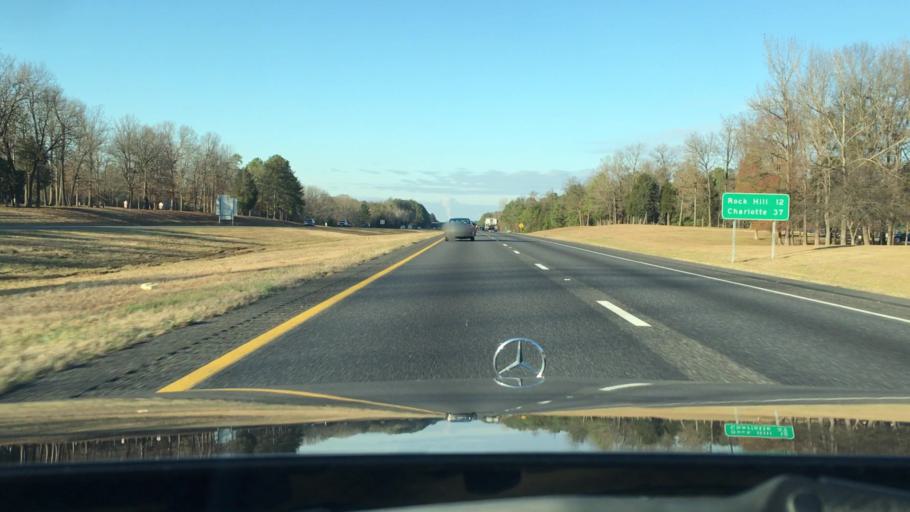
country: US
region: South Carolina
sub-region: York County
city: Lesslie
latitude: 34.7625
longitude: -81.0368
